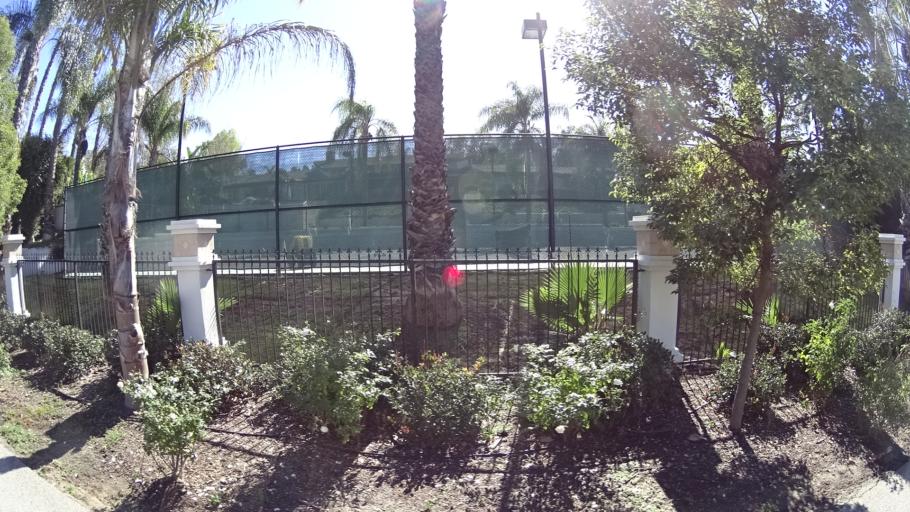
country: US
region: California
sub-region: Orange County
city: Villa Park
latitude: 33.8463
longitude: -117.8171
